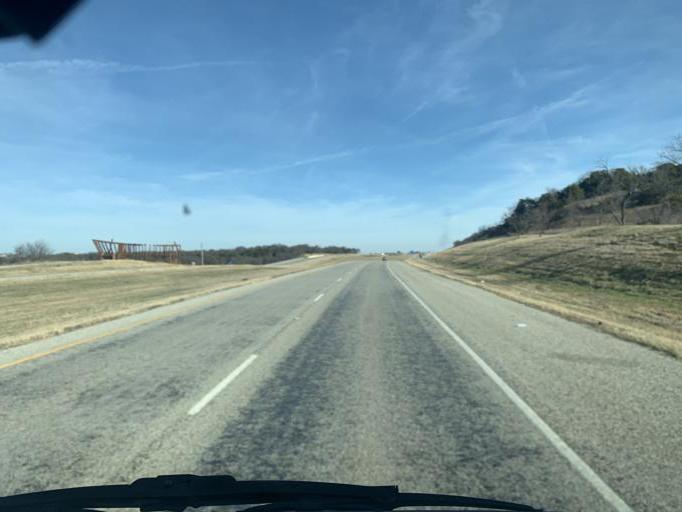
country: US
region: Texas
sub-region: Dallas County
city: Cedar Hill
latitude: 32.6232
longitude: -96.9759
